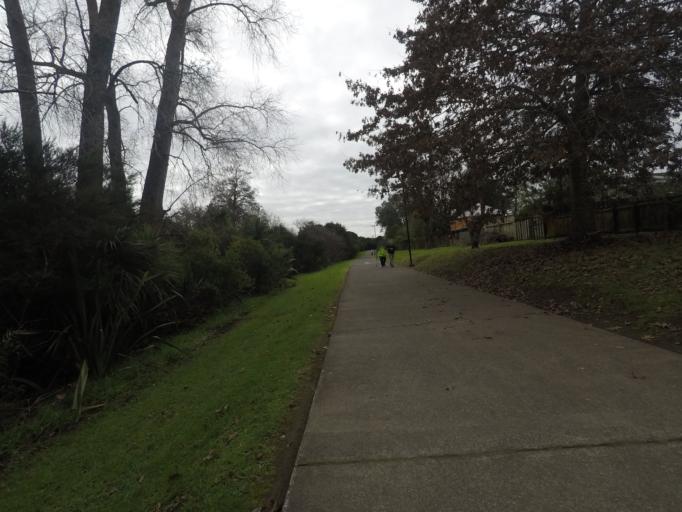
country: NZ
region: Auckland
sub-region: Auckland
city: Waitakere
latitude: -36.9011
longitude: 174.6263
